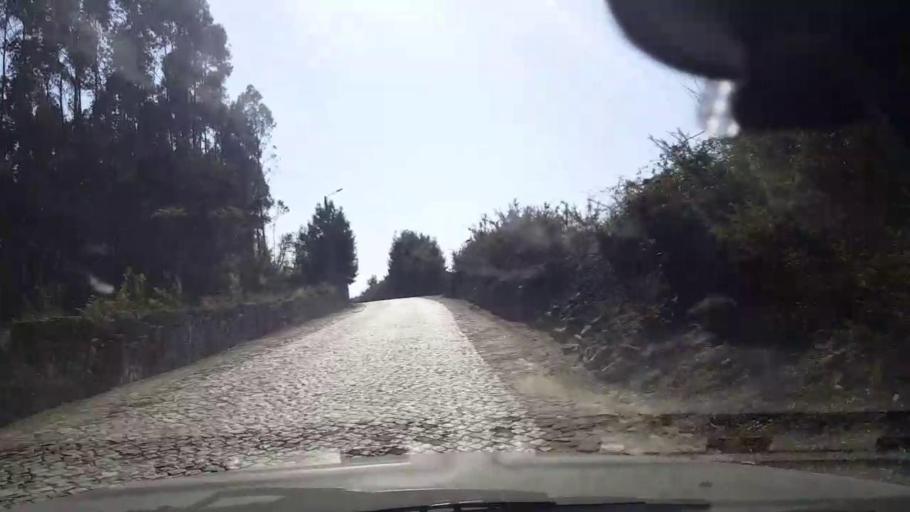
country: PT
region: Porto
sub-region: Vila do Conde
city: Arvore
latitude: 41.3546
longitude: -8.7030
